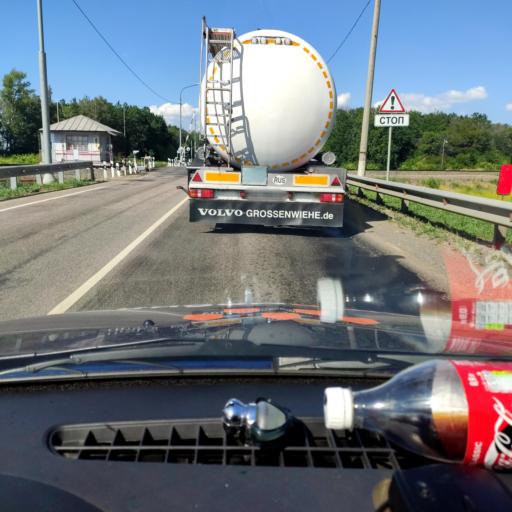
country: RU
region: Lipetsk
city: Kazaki
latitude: 52.5964
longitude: 38.2414
